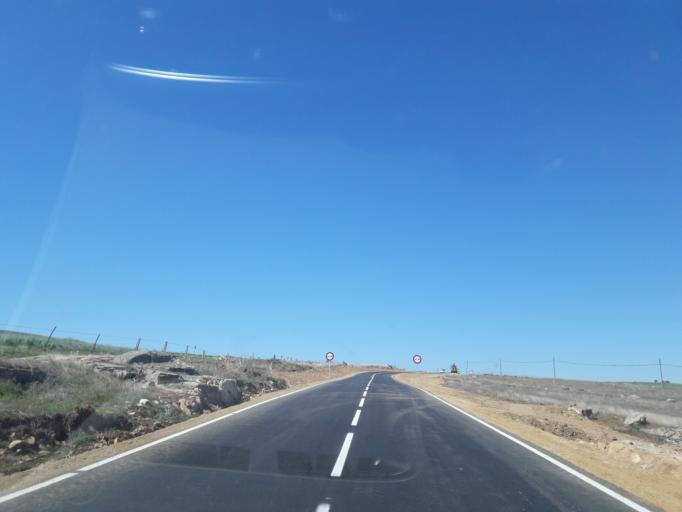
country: ES
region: Castille and Leon
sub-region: Provincia de Salamanca
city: Valdemierque
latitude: 40.8235
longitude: -5.5685
